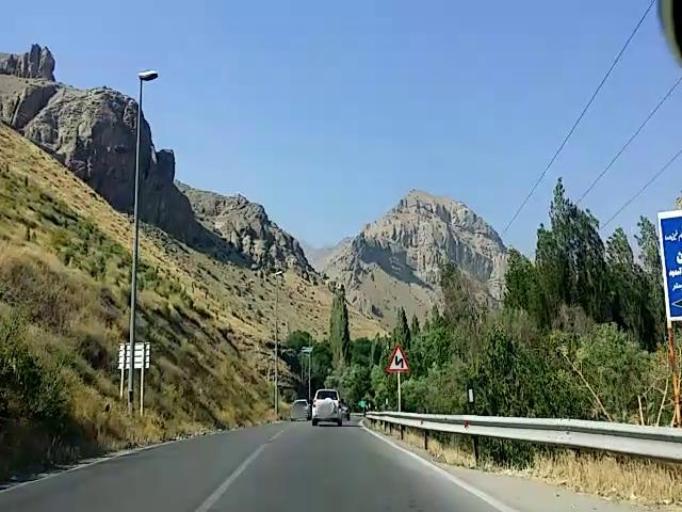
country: IR
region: Alborz
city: Karaj
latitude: 36.0207
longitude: 51.1507
